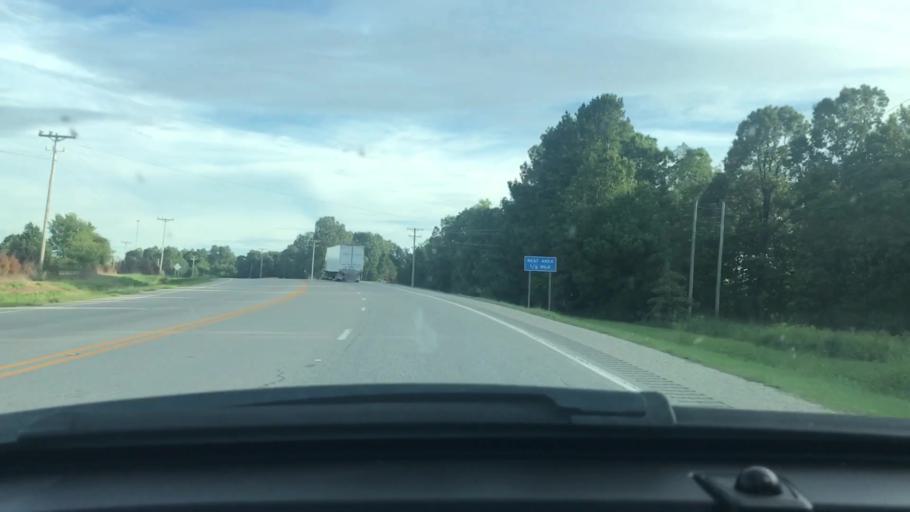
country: US
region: Arkansas
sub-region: Lawrence County
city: Hoxie
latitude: 36.1304
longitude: -91.1583
